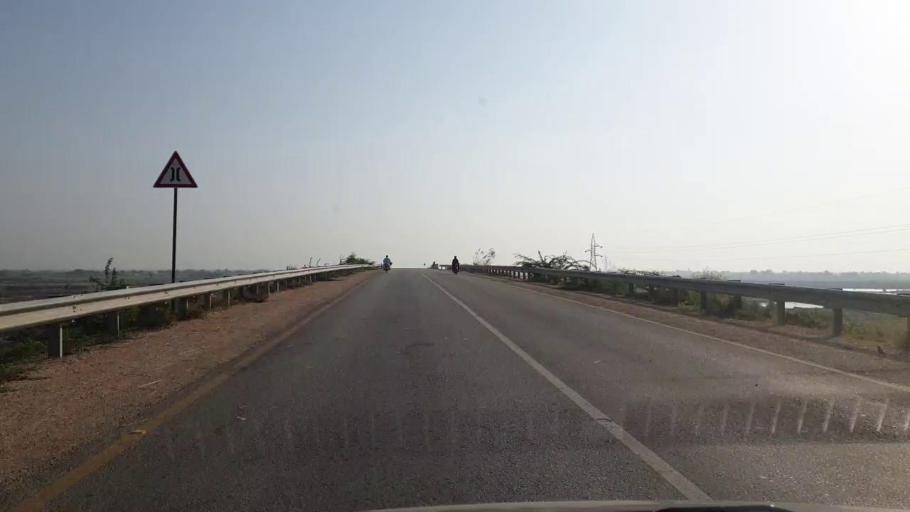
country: PK
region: Sindh
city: Badin
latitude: 24.6804
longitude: 68.8310
